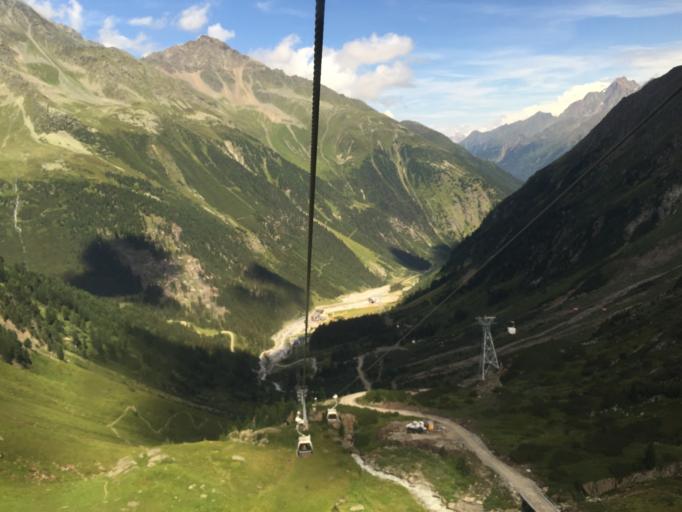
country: AT
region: Tyrol
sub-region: Politischer Bezirk Imst
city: Soelden
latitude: 47.0004
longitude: 11.1441
